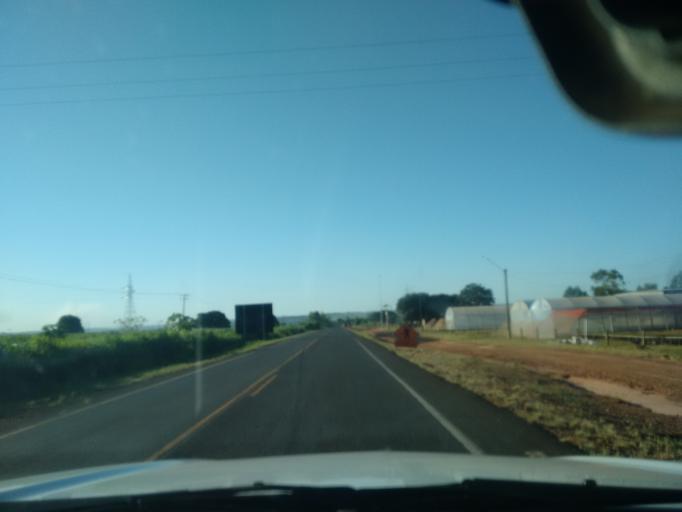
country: BR
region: Mato Grosso do Sul
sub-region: Eldorado
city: Eldorado
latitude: -23.8606
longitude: -54.3328
